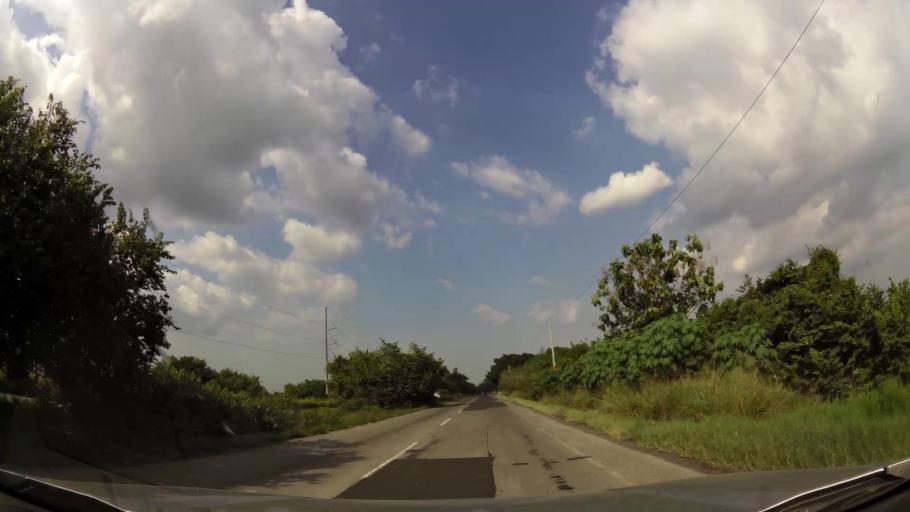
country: GT
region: Escuintla
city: Puerto San Jose
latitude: 14.0465
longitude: -90.7775
